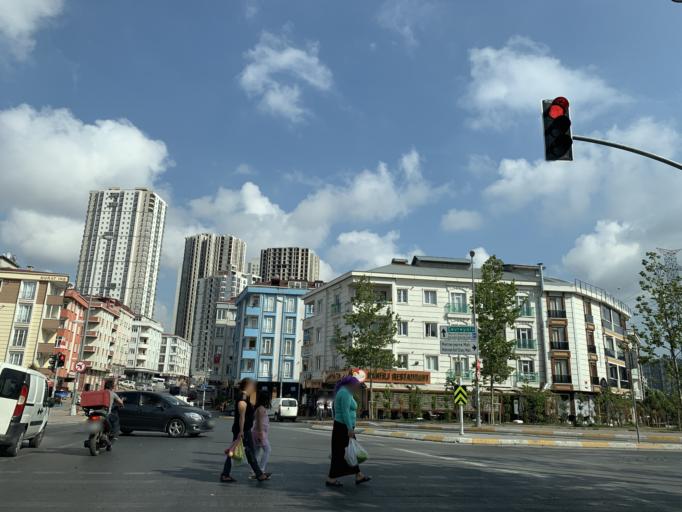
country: TR
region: Istanbul
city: Esenyurt
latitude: 41.0206
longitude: 28.6701
